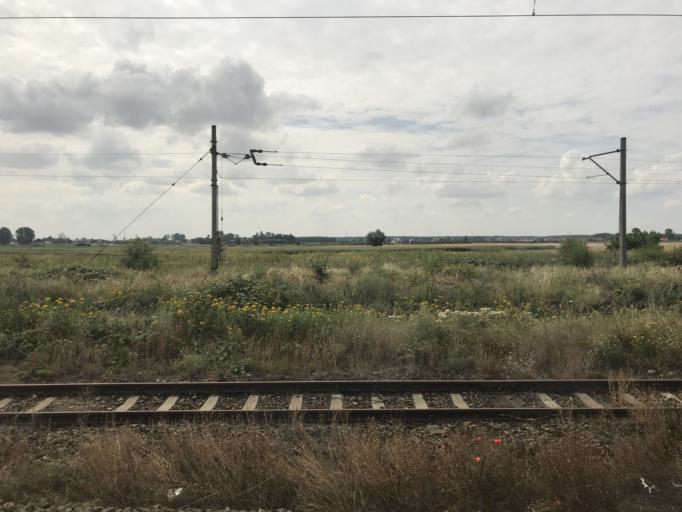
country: PL
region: Greater Poland Voivodeship
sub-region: Powiat gnieznienski
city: Gniezno
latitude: 52.5324
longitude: 17.6427
